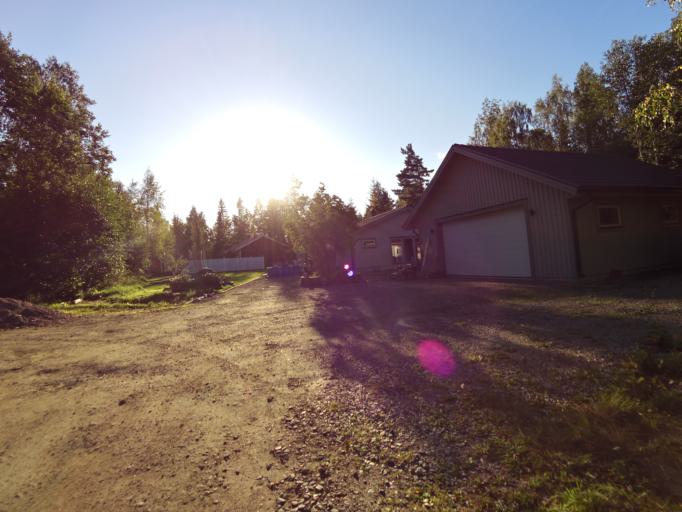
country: SE
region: Gaevleborg
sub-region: Gavle Kommun
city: Gavle
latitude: 60.7094
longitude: 17.1434
